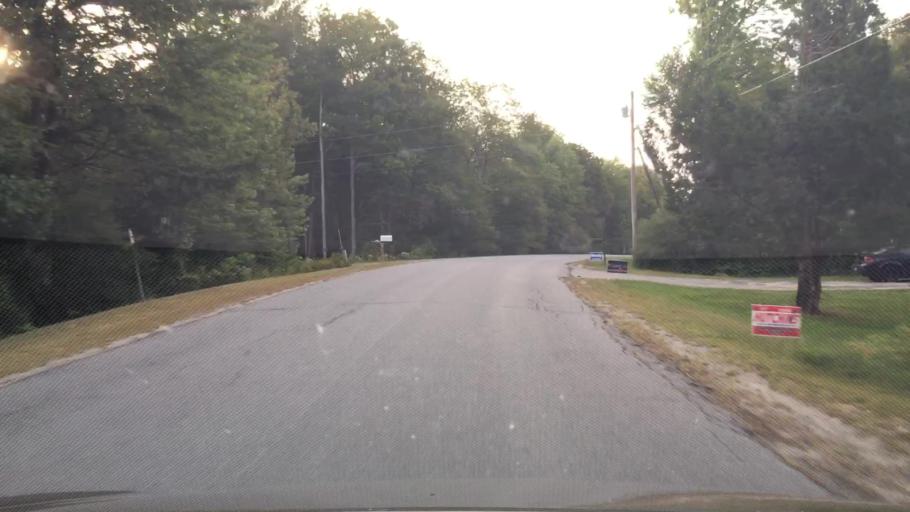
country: US
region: Maine
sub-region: Waldo County
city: Stockton Springs
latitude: 44.4925
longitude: -68.8696
